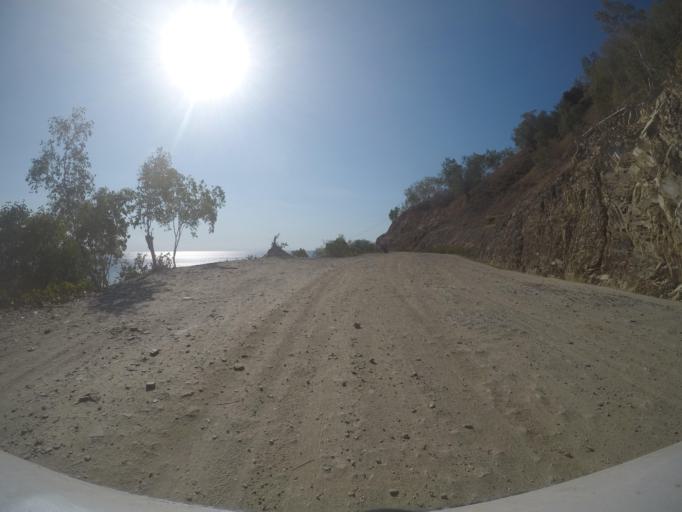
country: TL
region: Dili
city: Dili
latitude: -8.5366
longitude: 125.6165
